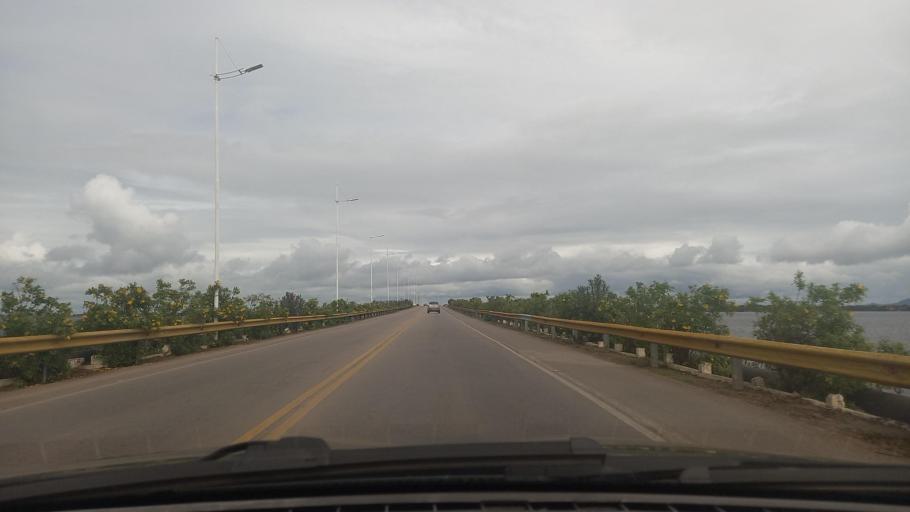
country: BR
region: Bahia
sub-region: Paulo Afonso
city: Paulo Afonso
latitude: -9.4199
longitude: -38.2318
